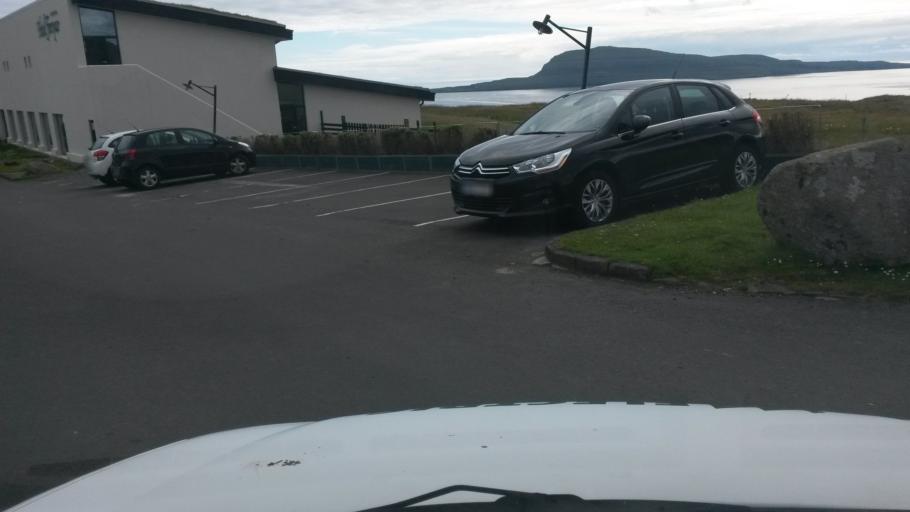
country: FO
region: Streymoy
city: Hoyvik
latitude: 62.0123
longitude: -6.8009
